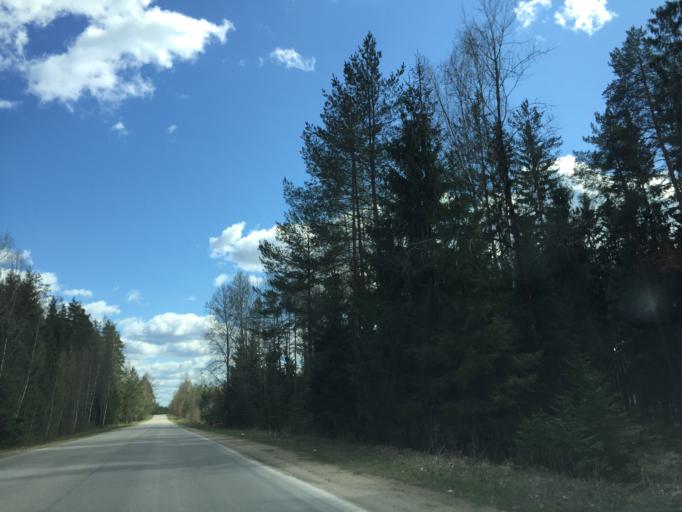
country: LV
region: Vilanu
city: Vilani
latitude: 56.5678
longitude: 27.0499
